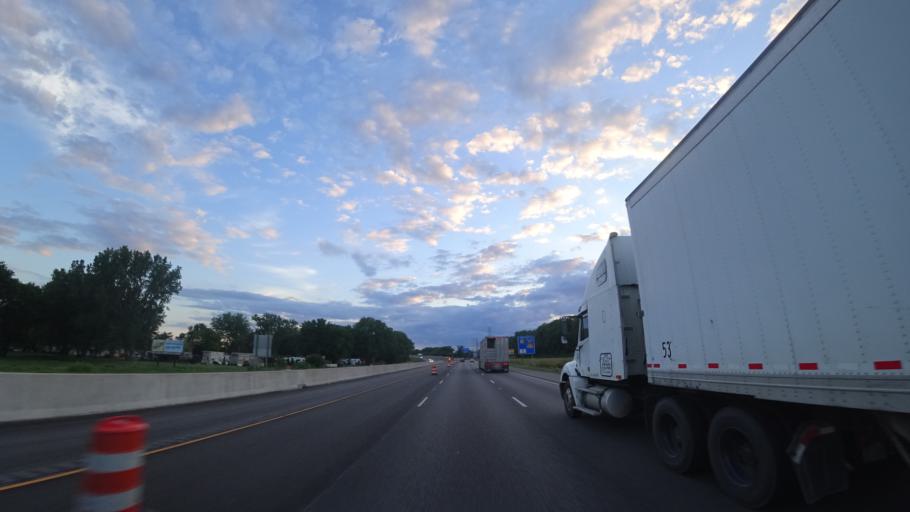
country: US
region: Indiana
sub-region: Porter County
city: Ogden Dunes
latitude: 41.5978
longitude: -87.2068
